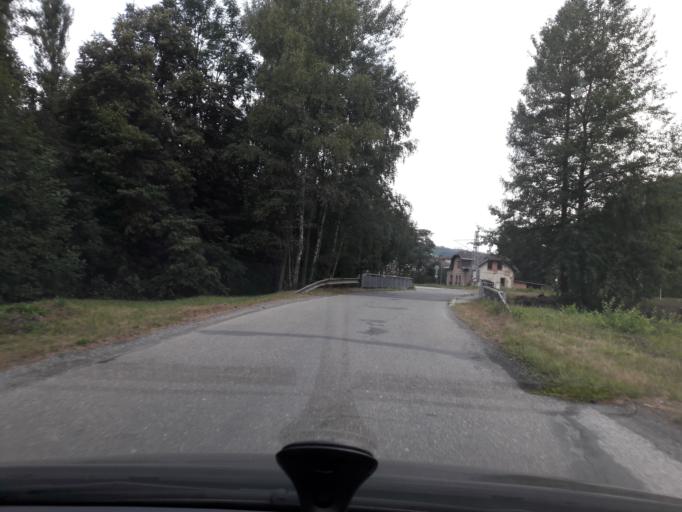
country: CZ
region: Olomoucky
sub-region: Okres Sumperk
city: Loucna nad Desnou
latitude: 50.0698
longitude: 17.0867
